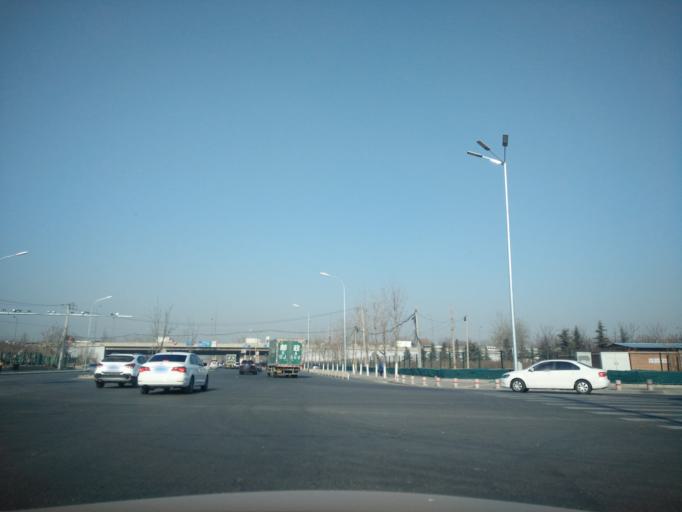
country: CN
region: Beijing
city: Jiugong
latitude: 39.8198
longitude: 116.5077
